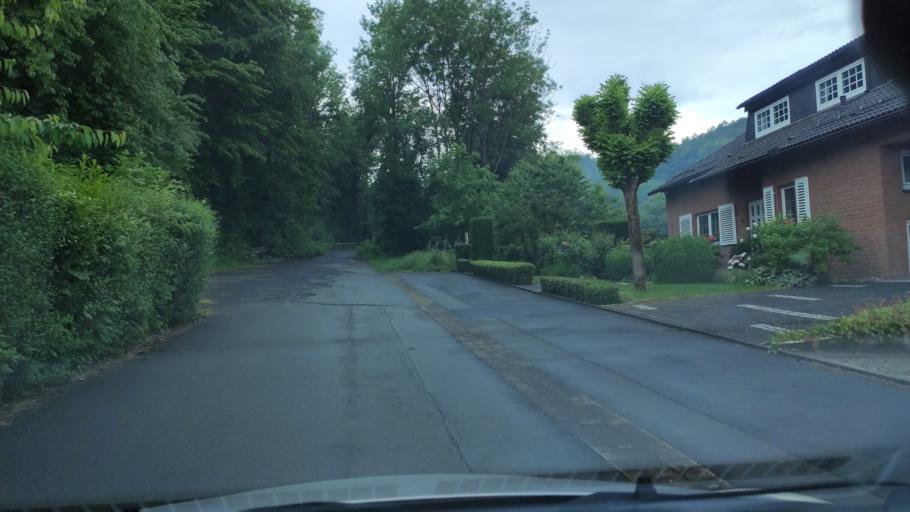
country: DE
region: North Rhine-Westphalia
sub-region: Regierungsbezirk Detmold
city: Hoexter
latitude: 51.7670
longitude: 9.3607
